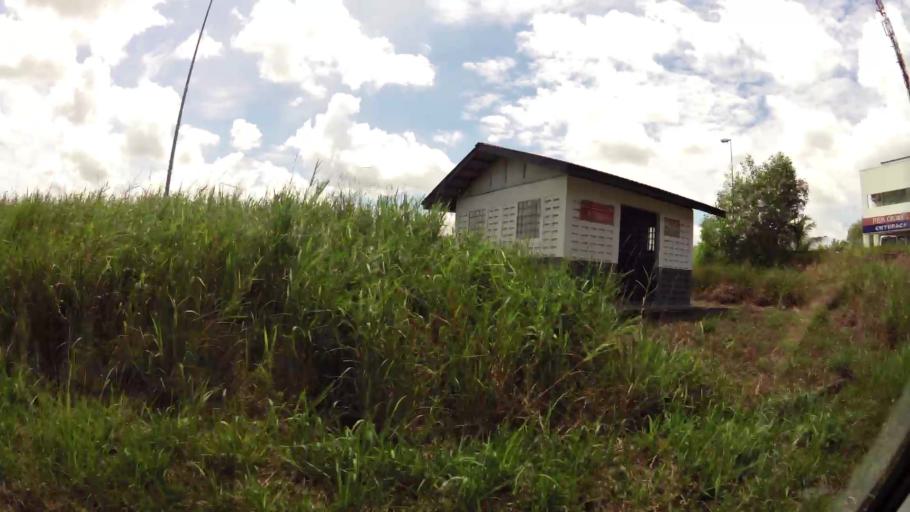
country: BN
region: Brunei and Muara
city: Bandar Seri Begawan
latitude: 4.9429
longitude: 114.9066
